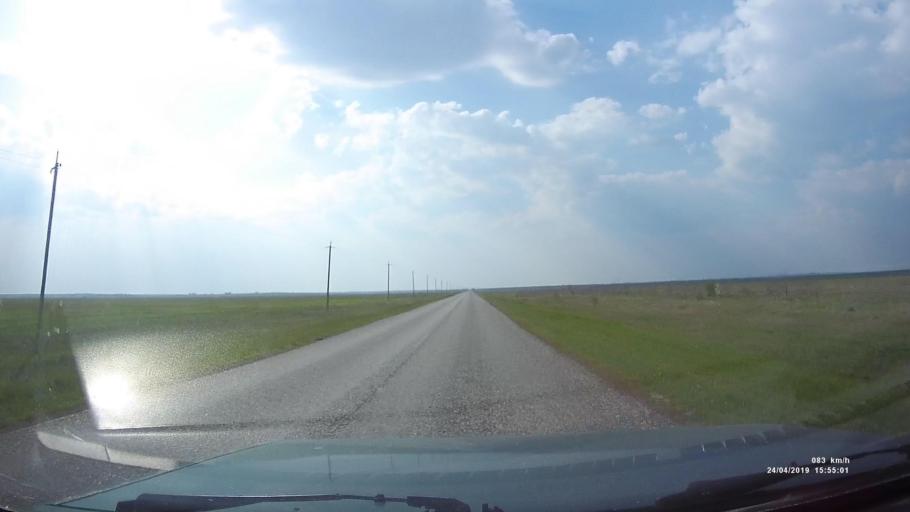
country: RU
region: Kalmykiya
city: Yashalta
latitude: 46.5876
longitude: 42.5573
